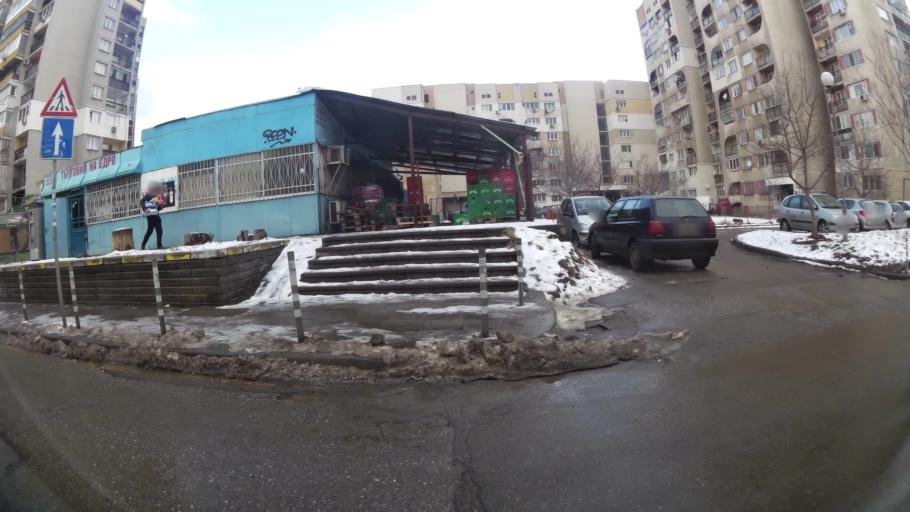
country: BG
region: Sofia-Capital
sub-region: Stolichna Obshtina
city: Sofia
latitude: 42.6978
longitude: 23.2864
